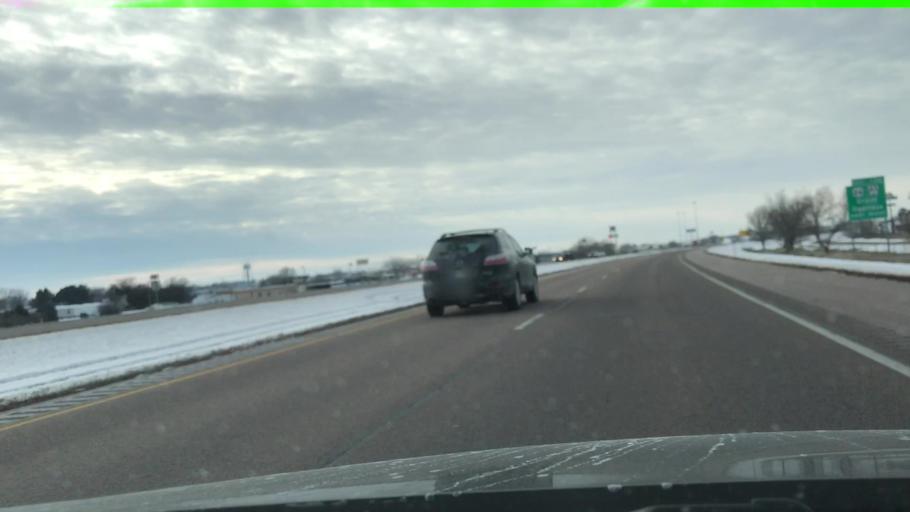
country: US
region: Nebraska
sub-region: Keith County
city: Ogallala
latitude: 41.1156
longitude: -101.7031
